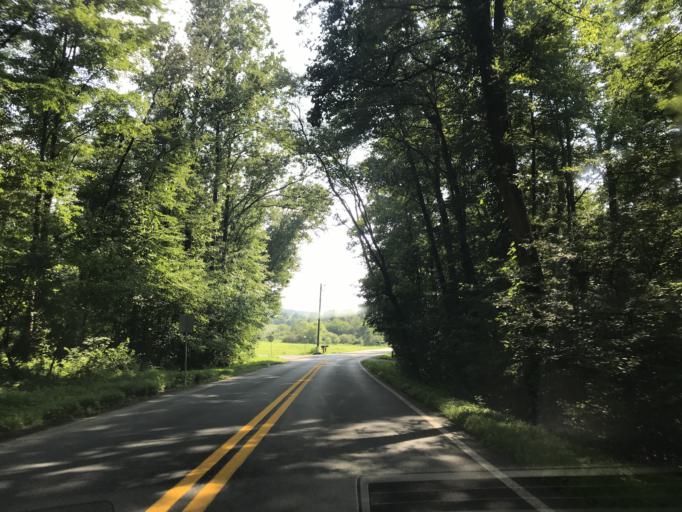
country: US
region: Maryland
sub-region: Carroll County
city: Manchester
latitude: 39.6346
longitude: -76.9508
